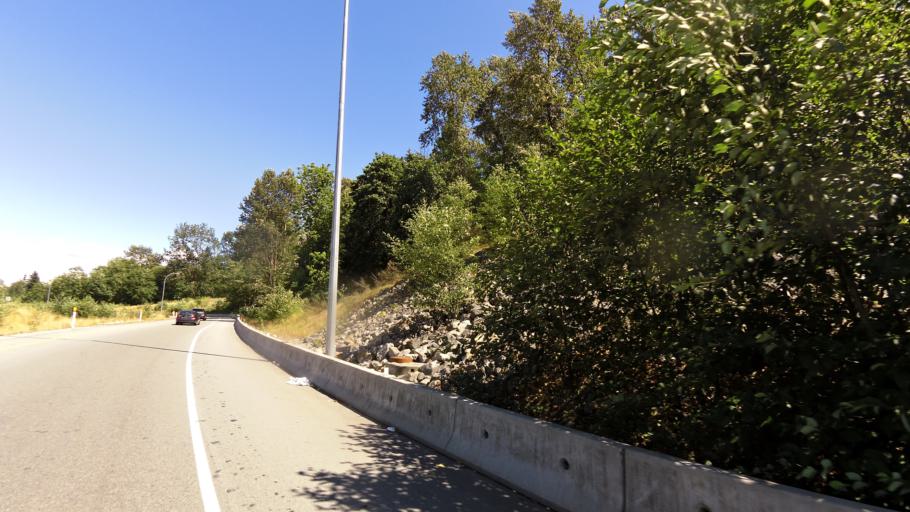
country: CA
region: British Columbia
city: New Westminster
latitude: 49.2408
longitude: -122.9169
